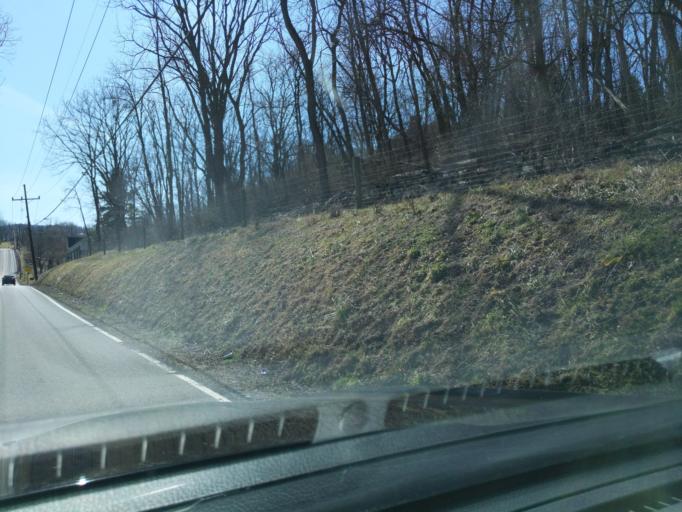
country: US
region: Pennsylvania
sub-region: Blair County
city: Duncansville
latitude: 40.4203
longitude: -78.4214
